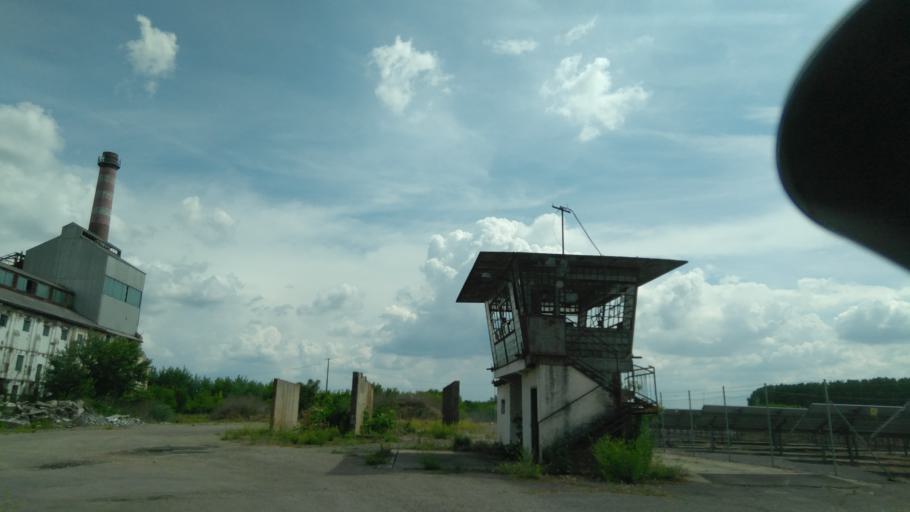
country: HU
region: Bekes
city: Mezohegyes
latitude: 46.3104
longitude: 20.8069
